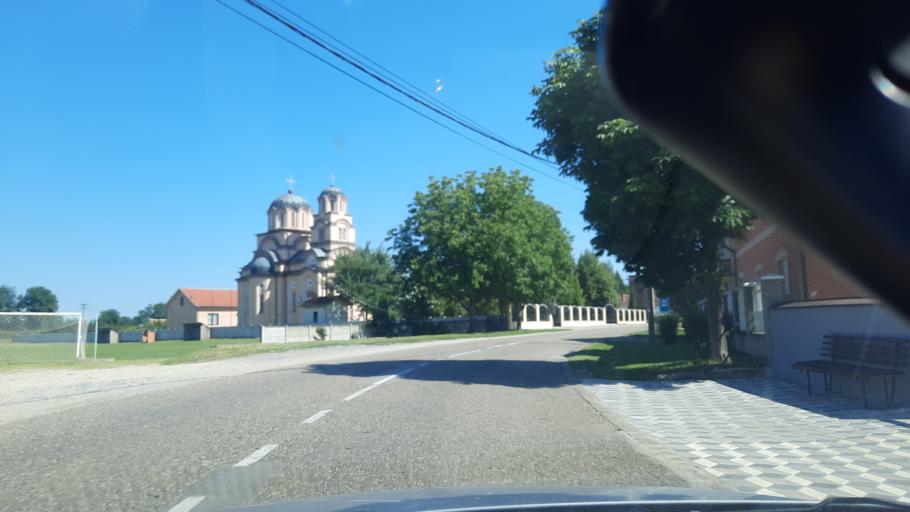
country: RS
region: Central Serbia
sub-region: Branicevski Okrug
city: Malo Crnice
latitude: 44.6136
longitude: 21.2673
